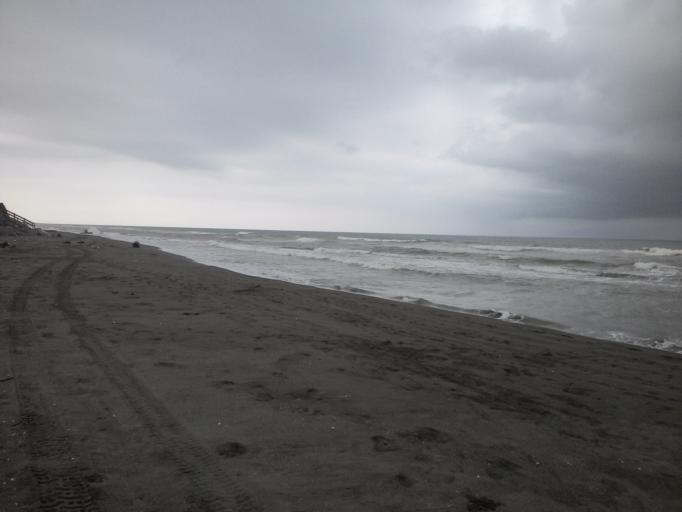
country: MX
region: Veracruz
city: Nautla
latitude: 20.2136
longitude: -96.7598
